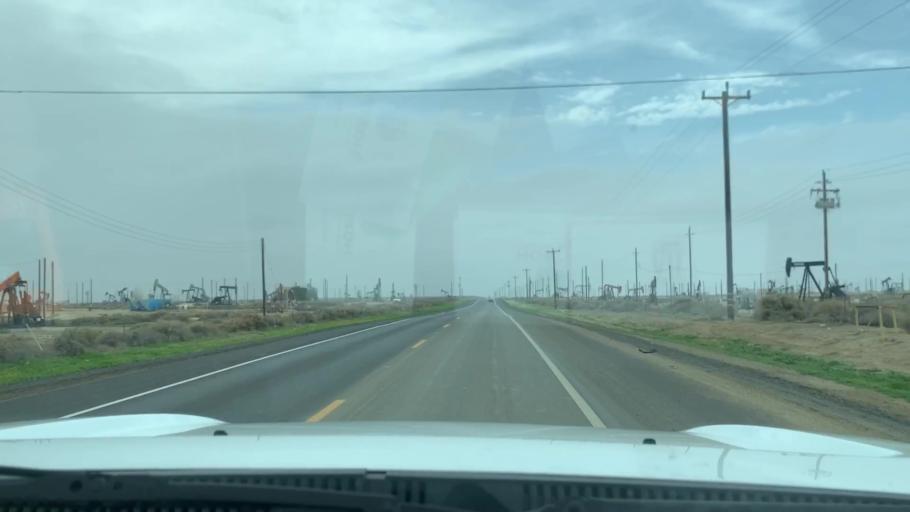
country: US
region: California
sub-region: Kern County
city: Lost Hills
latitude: 35.6159
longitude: -119.7264
